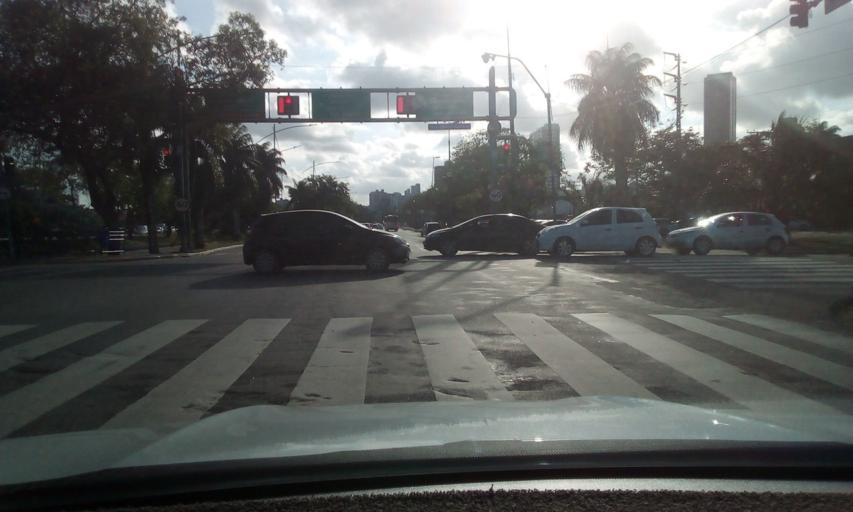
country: BR
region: Pernambuco
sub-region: Recife
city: Recife
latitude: -8.0395
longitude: -34.8788
